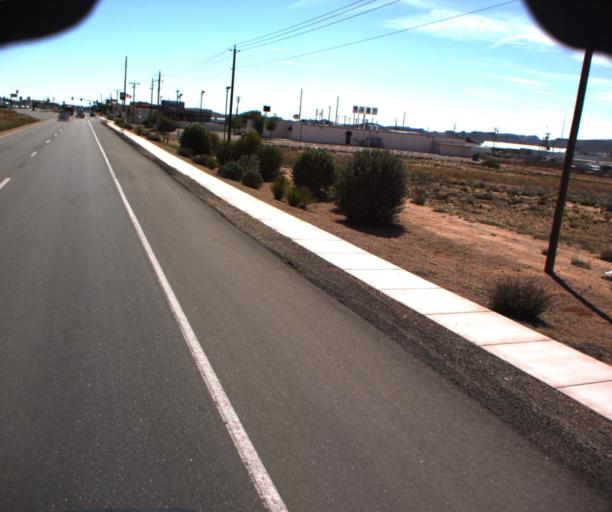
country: US
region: Arizona
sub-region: Mohave County
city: New Kingman-Butler
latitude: 35.2264
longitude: -114.0021
